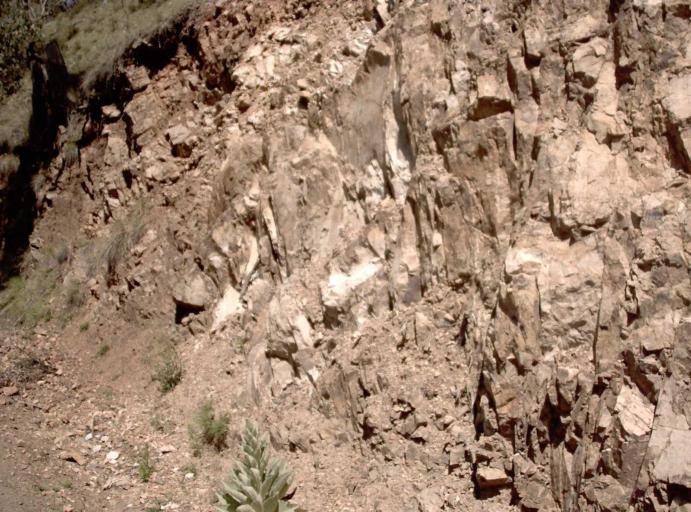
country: AU
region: New South Wales
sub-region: Bombala
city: Bombala
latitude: -37.1047
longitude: 148.6382
